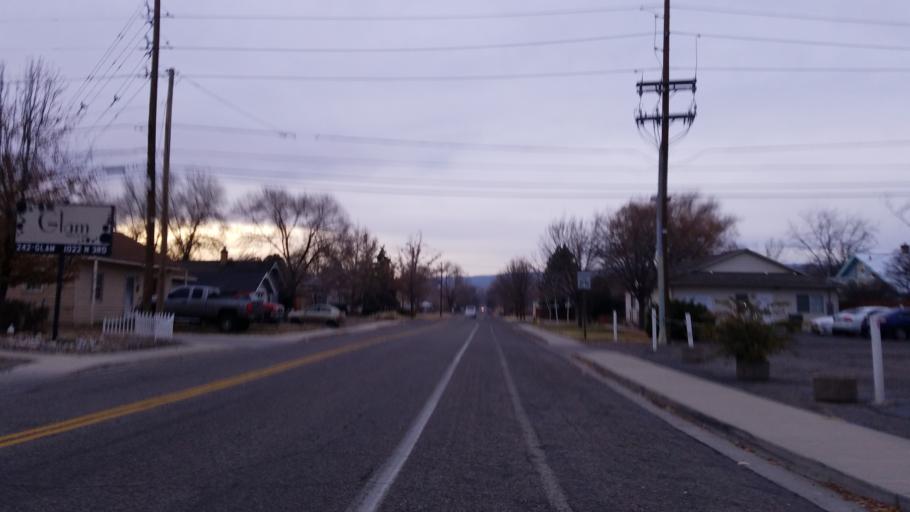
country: US
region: Colorado
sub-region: Mesa County
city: Grand Junction
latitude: 39.0772
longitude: -108.5679
